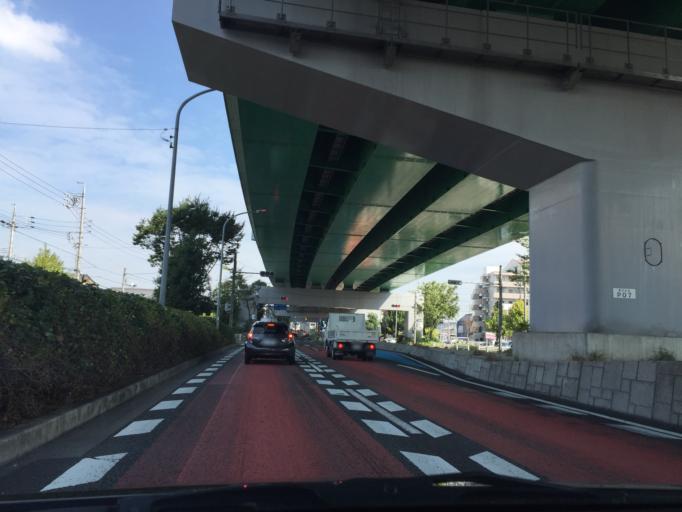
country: JP
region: Aichi
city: Ichinomiya
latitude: 35.3047
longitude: 136.7738
